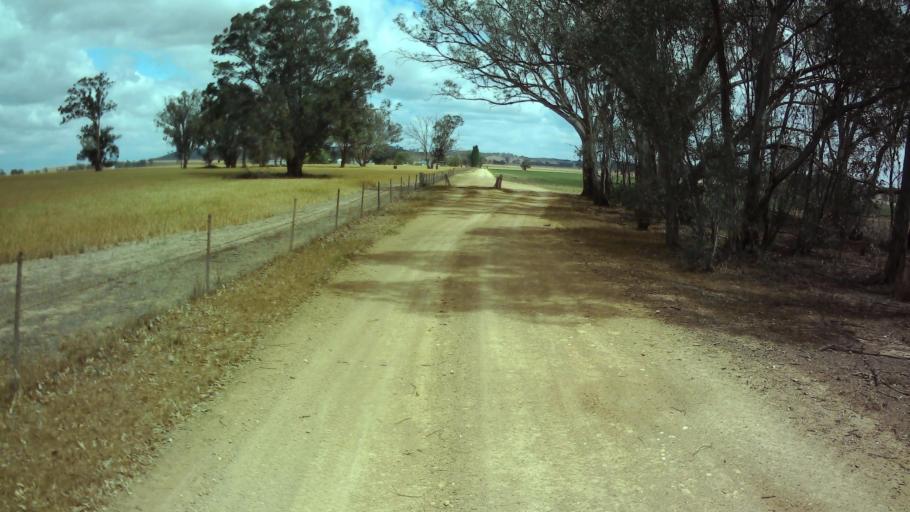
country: AU
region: New South Wales
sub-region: Weddin
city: Grenfell
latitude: -33.9795
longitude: 148.2657
